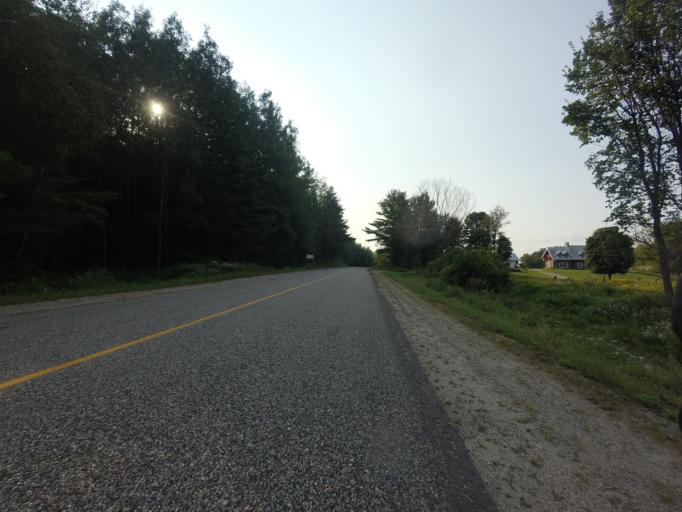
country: CA
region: Ontario
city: Perth
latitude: 44.9267
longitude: -76.6810
